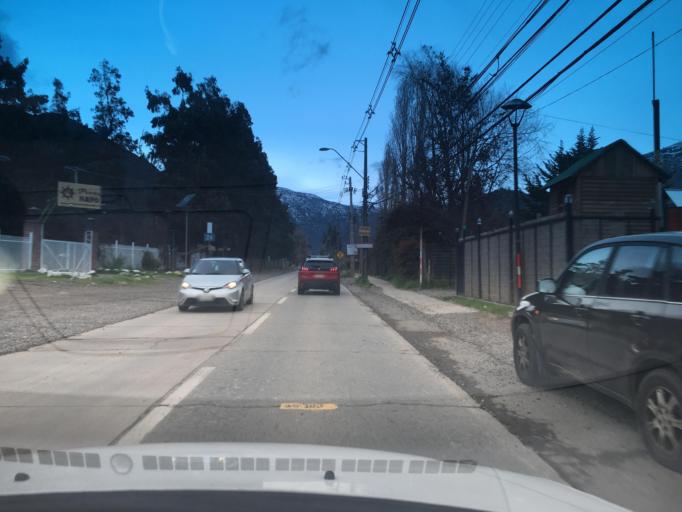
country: CL
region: Santiago Metropolitan
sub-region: Provincia de Cordillera
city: Puente Alto
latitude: -33.5853
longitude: -70.3941
